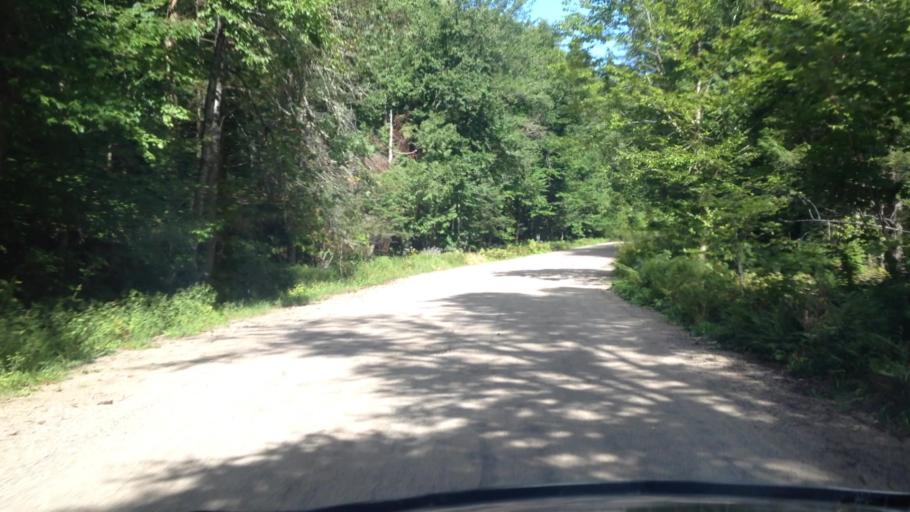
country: CA
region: Quebec
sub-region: Laurentides
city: Mont-Tremblant
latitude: 45.9249
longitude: -74.5832
